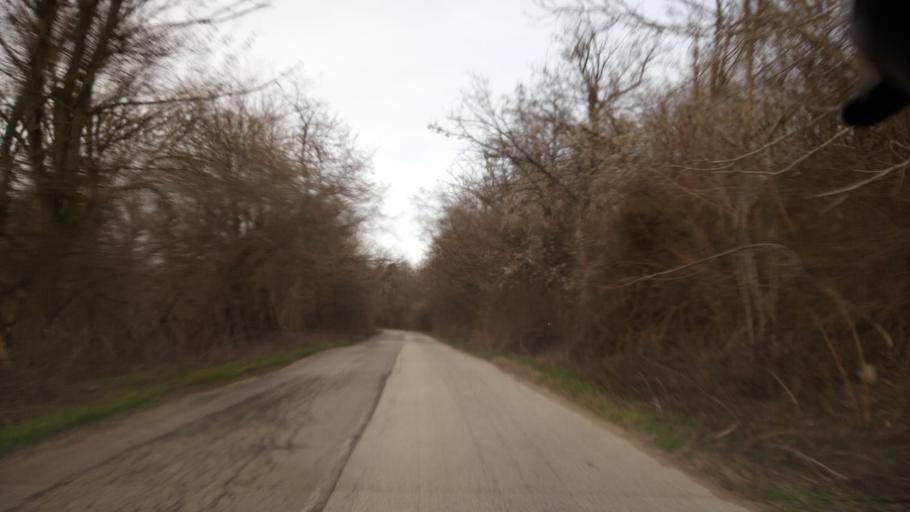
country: BG
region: Pleven
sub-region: Obshtina Nikopol
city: Nikopol
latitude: 43.5972
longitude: 24.9797
